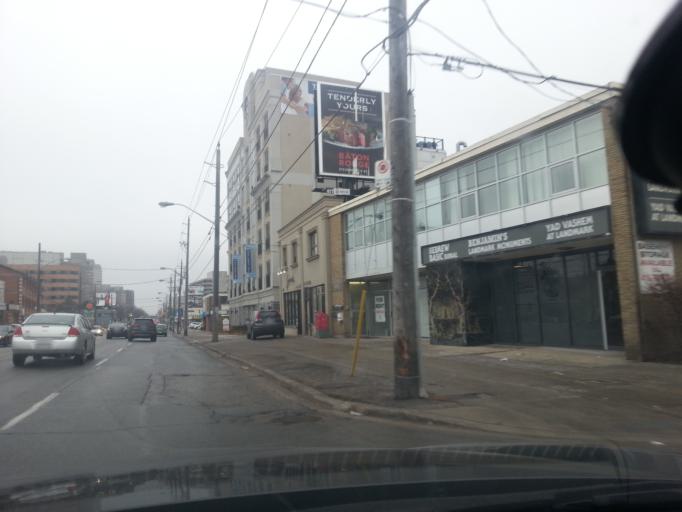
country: CA
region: Ontario
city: Toronto
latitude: 43.7274
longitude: -79.4316
